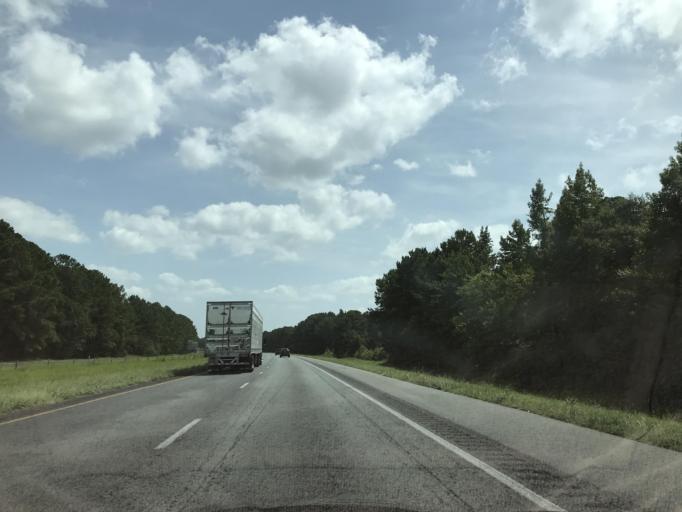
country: US
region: North Carolina
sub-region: Duplin County
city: Warsaw
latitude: 34.9777
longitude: -78.1275
